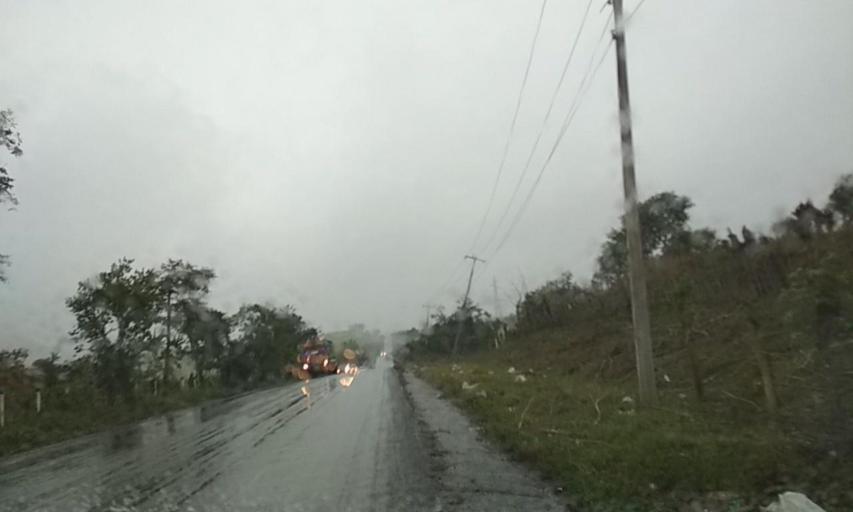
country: MX
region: Veracruz
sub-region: Papantla
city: El Chote
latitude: 20.3941
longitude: -97.3289
